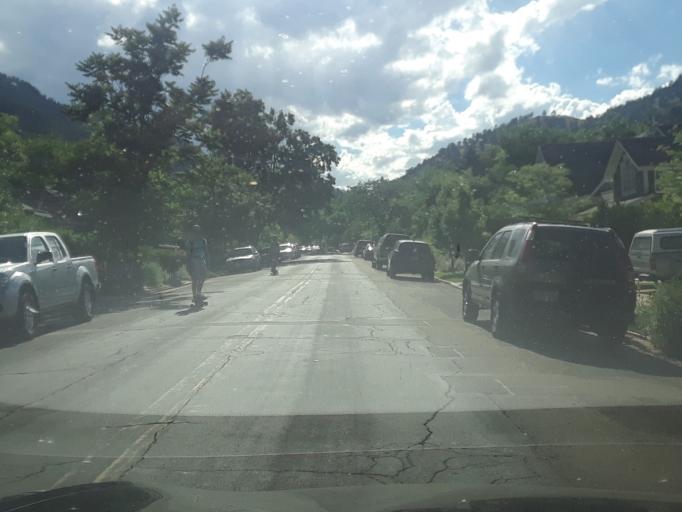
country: US
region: Colorado
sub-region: Boulder County
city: Boulder
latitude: 40.0130
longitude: -105.2901
